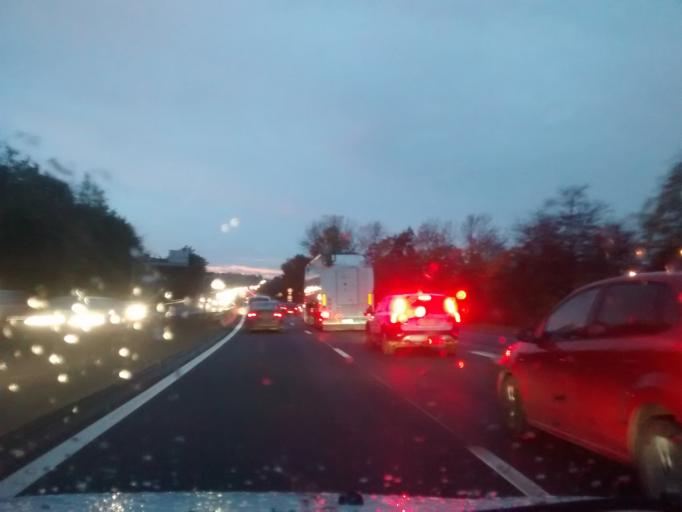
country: FR
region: Brittany
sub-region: Departement des Cotes-d'Armor
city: Saint-Brieuc
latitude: 48.5162
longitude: -2.7438
